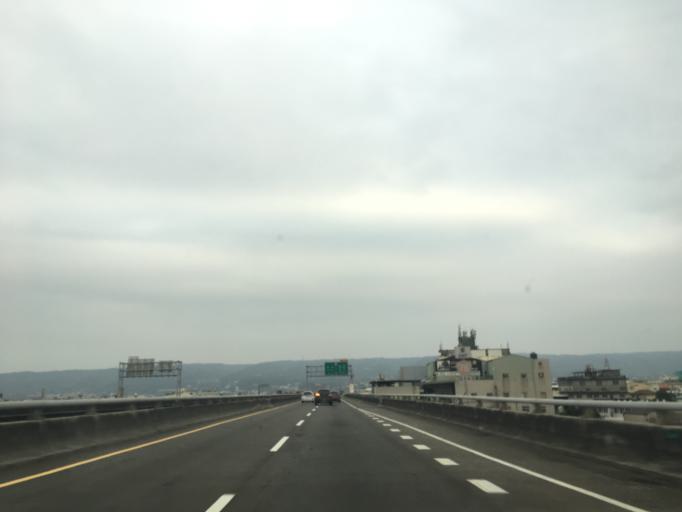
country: TW
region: Taiwan
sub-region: Nantou
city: Nantou
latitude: 23.9443
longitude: 120.5726
